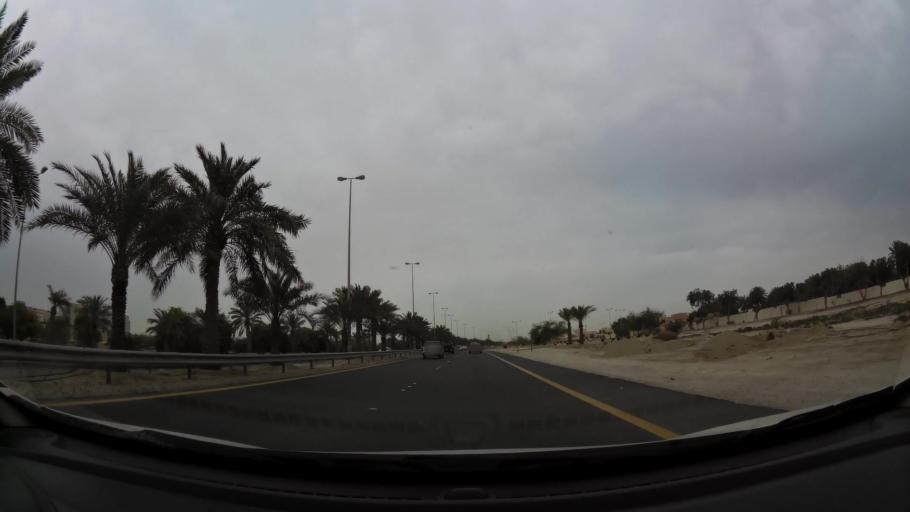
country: BH
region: Northern
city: Ar Rifa'
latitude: 26.1421
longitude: 50.5395
